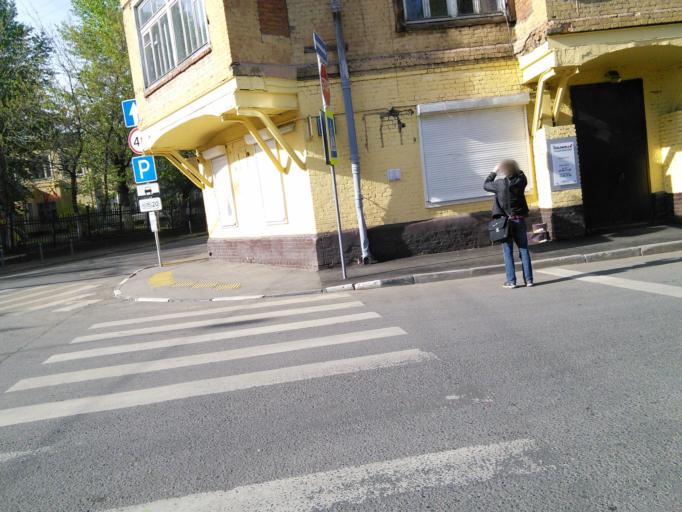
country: RU
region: Moskovskaya
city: Dorogomilovo
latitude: 55.7588
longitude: 37.5634
